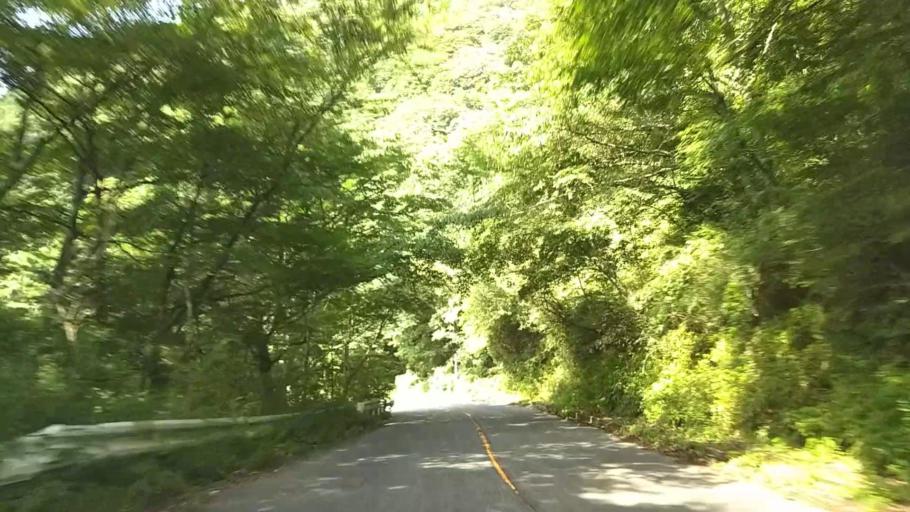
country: JP
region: Kanagawa
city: Hakone
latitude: 35.2256
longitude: 139.0042
